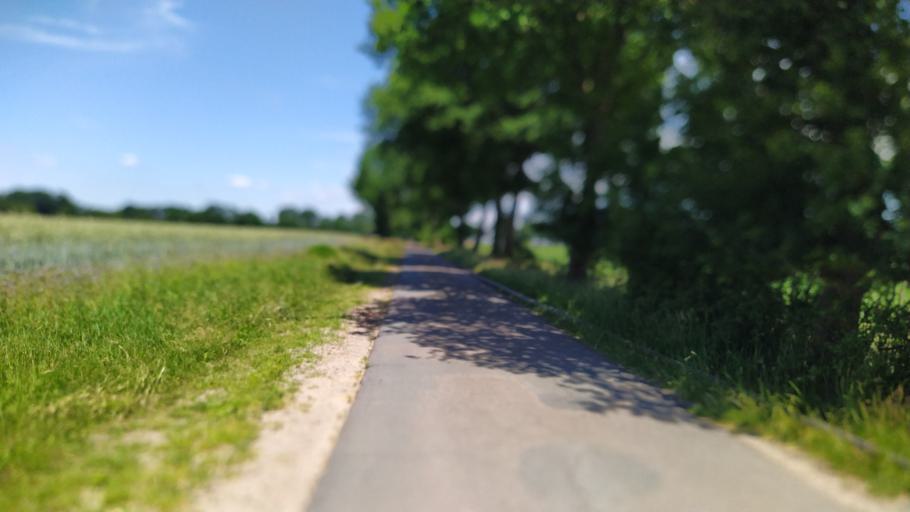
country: DE
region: Lower Saxony
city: Deinste
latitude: 53.5123
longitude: 9.4399
